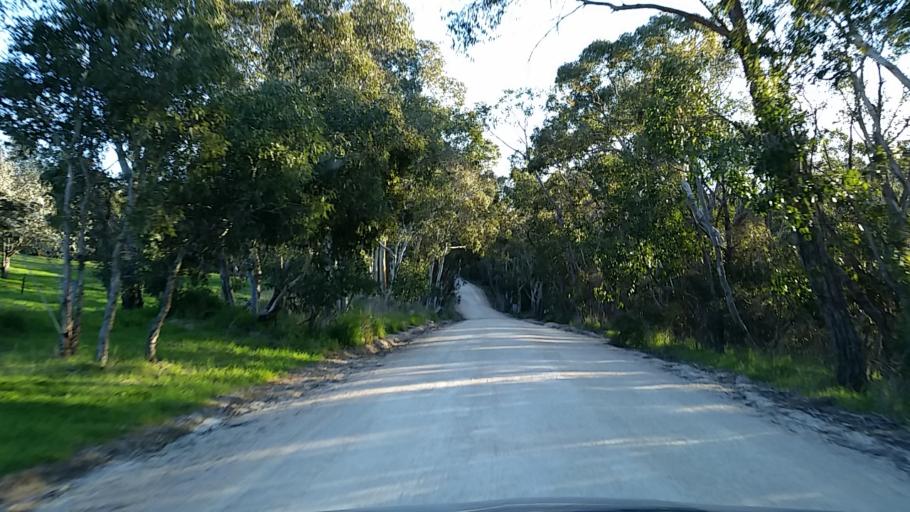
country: AU
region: South Australia
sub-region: Alexandrina
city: Mount Compass
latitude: -35.2969
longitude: 138.6842
